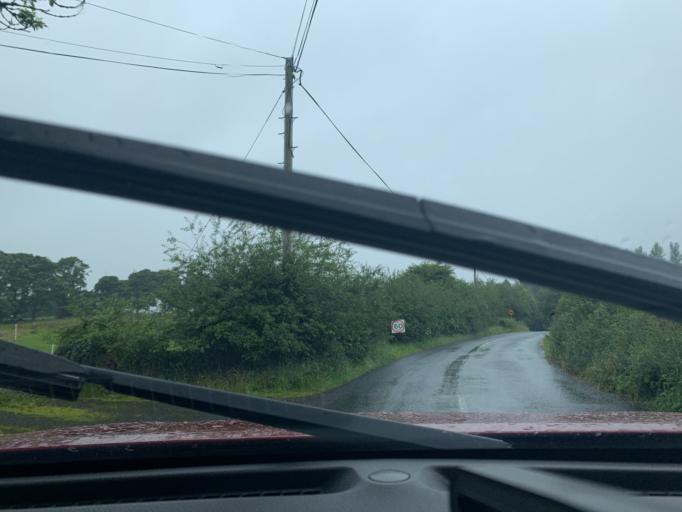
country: IE
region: Connaught
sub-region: County Leitrim
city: Manorhamilton
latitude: 54.2856
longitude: -7.9185
